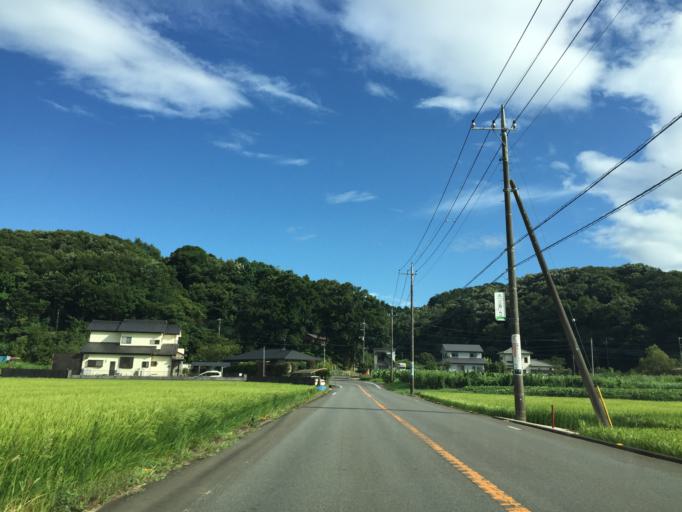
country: JP
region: Shizuoka
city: Mishima
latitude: 35.1672
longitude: 138.9230
